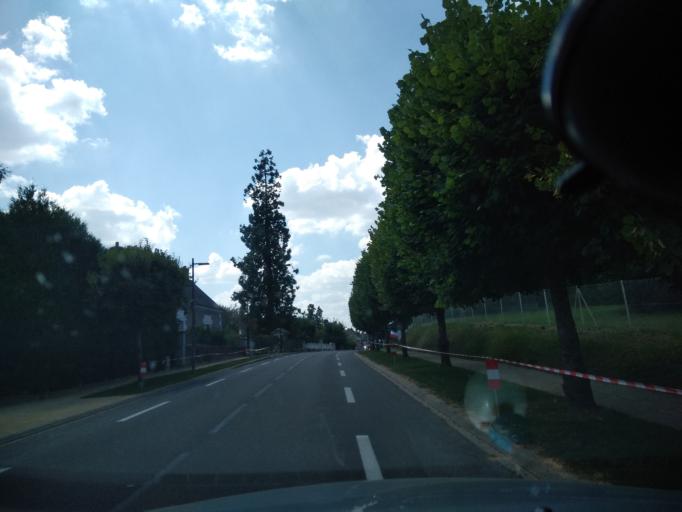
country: FR
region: Centre
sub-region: Departement d'Indre-et-Loire
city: Civray-de-Touraine
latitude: 47.3316
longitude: 1.0735
